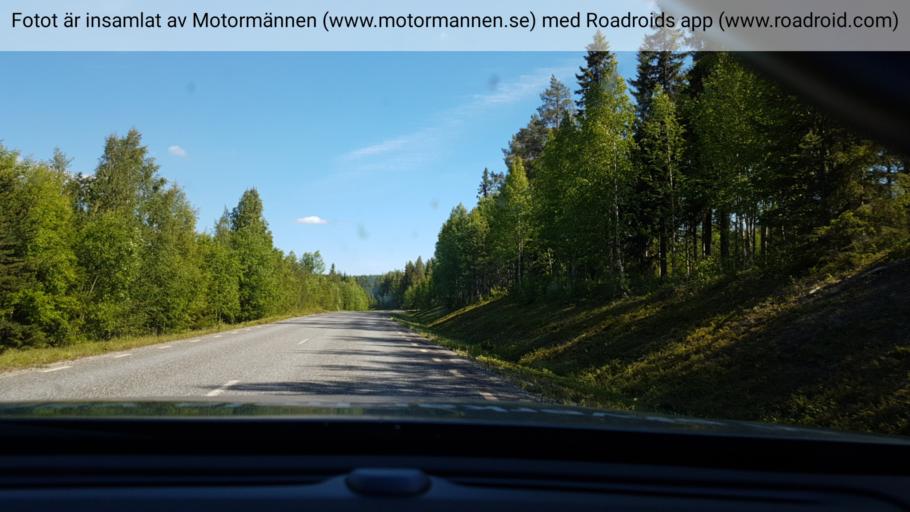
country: SE
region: Vaesterbotten
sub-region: Lycksele Kommun
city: Lycksele
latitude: 64.6157
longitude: 18.4388
